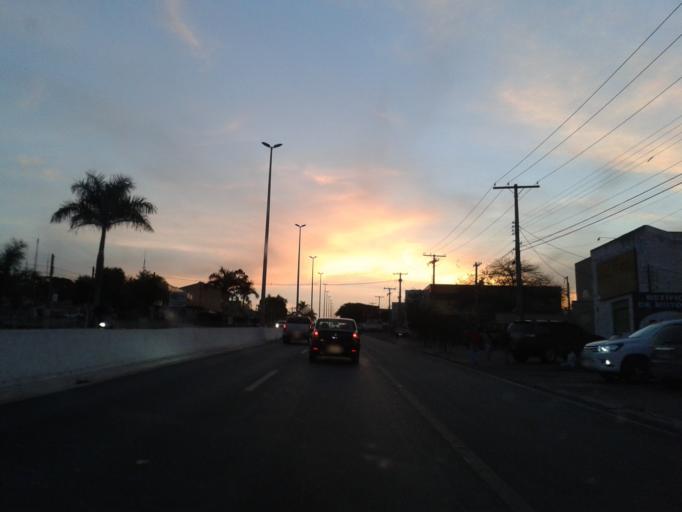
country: BR
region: Goias
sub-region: Goiania
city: Goiania
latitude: -16.6601
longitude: -49.3335
